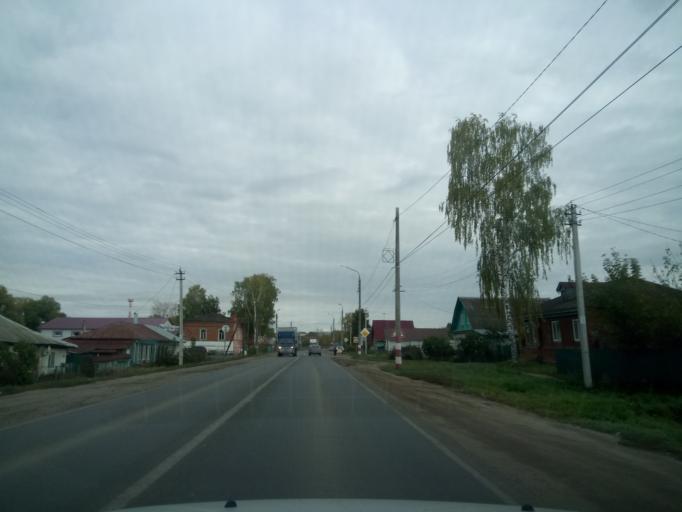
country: RU
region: Nizjnij Novgorod
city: Lukoyanov
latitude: 55.0306
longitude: 44.4860
